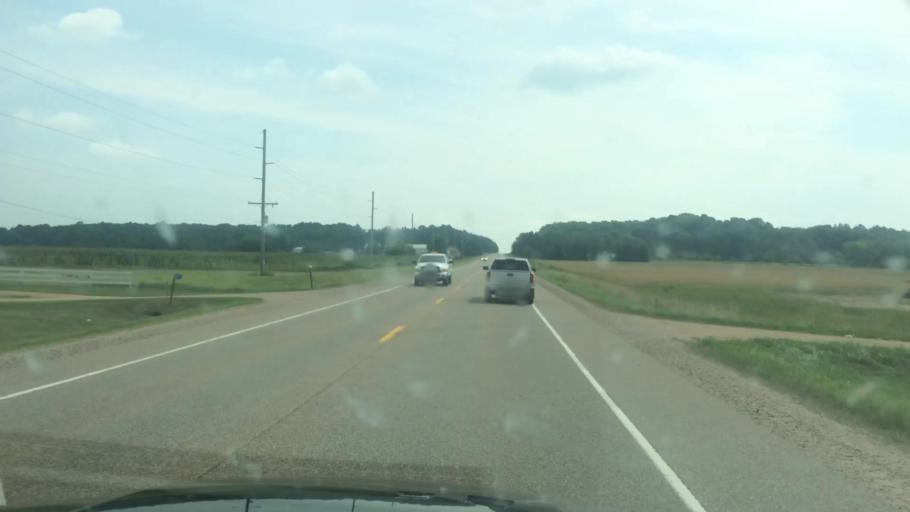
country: US
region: Wisconsin
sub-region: Langlade County
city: Antigo
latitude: 45.1620
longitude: -89.0718
